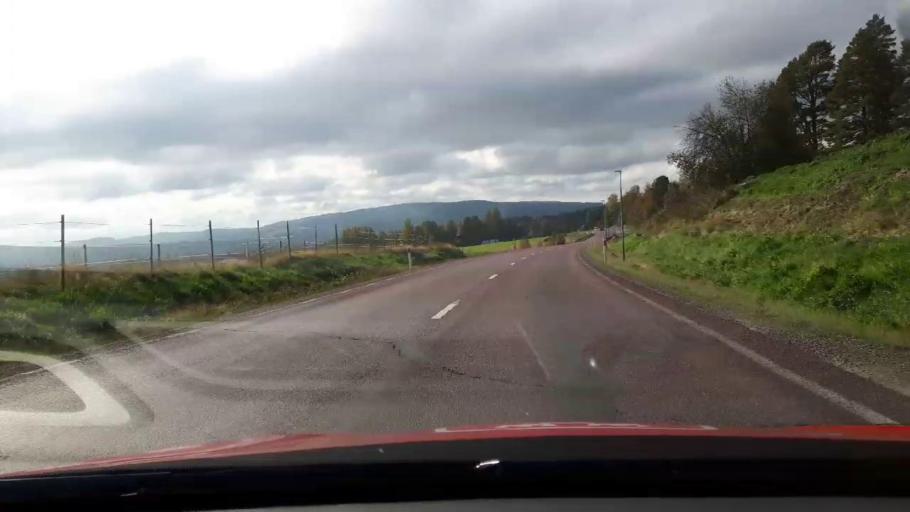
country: SE
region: Gaevleborg
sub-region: Ljusdals Kommun
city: Jaervsoe
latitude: 61.6977
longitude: 16.1610
